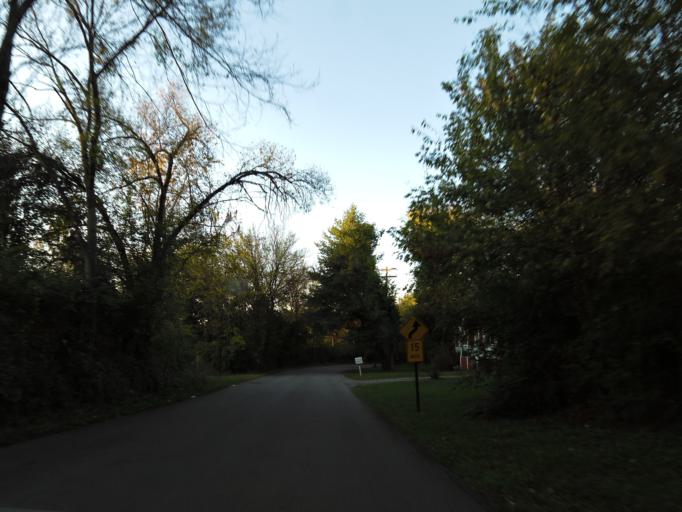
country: US
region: Tennessee
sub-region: Blount County
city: Alcoa
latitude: 35.7861
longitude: -83.9555
